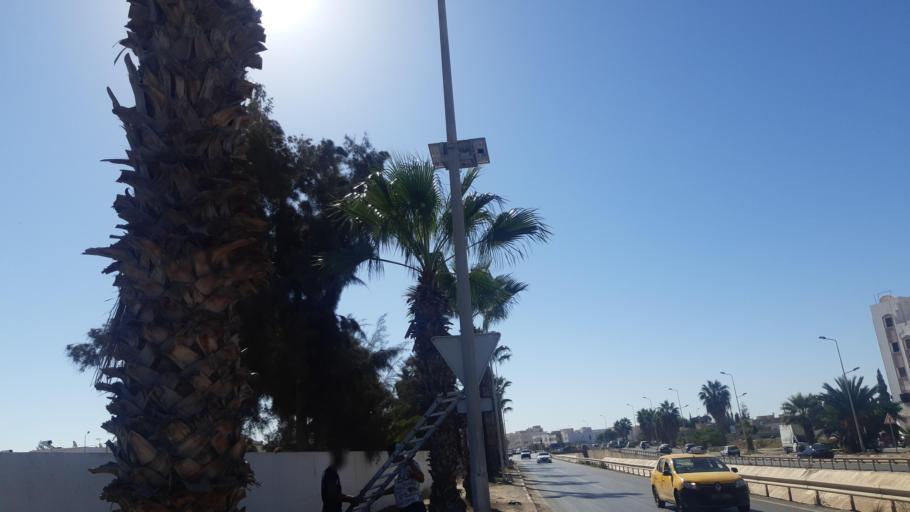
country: TN
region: Safaqis
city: Sfax
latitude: 34.7253
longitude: 10.7269
